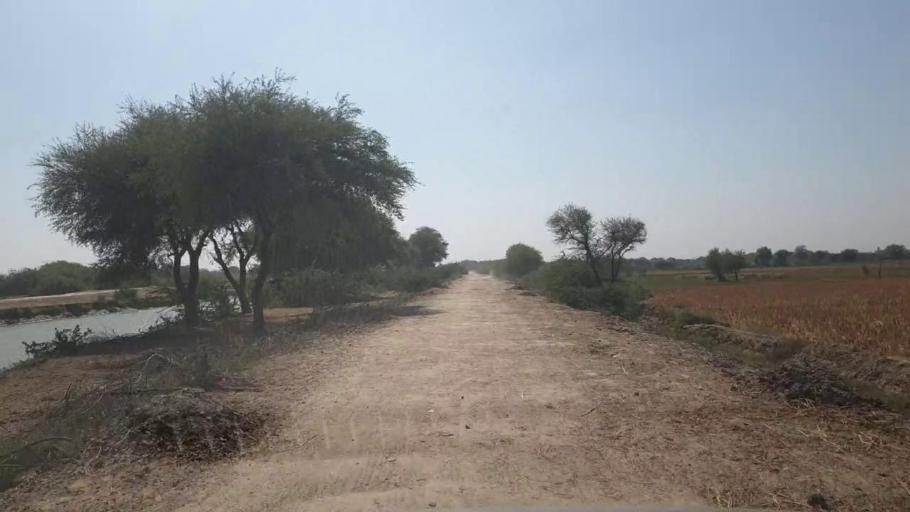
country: PK
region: Sindh
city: Talhar
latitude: 24.8238
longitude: 68.7942
